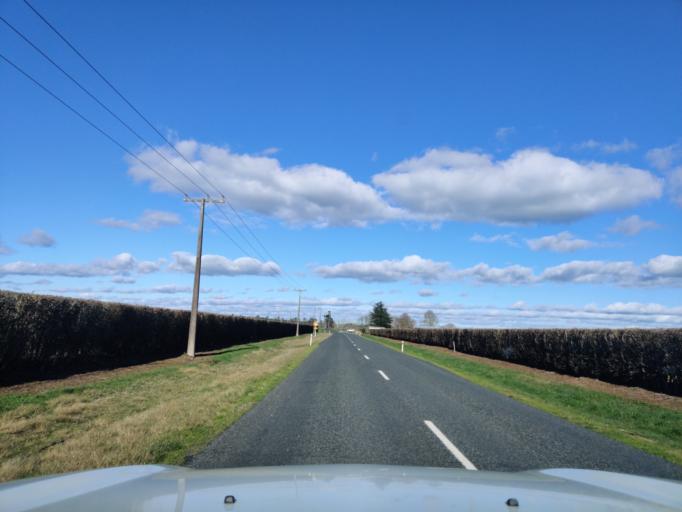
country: NZ
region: Waikato
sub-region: Matamata-Piako District
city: Matamata
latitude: -37.8809
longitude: 175.7305
